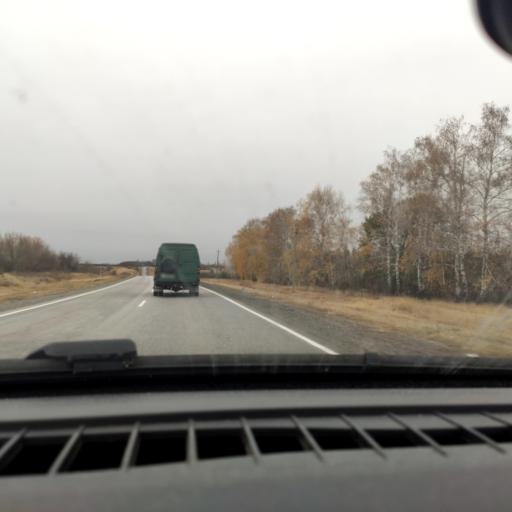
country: RU
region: Voronezj
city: Uryv-Pokrovka
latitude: 51.0669
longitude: 38.9956
